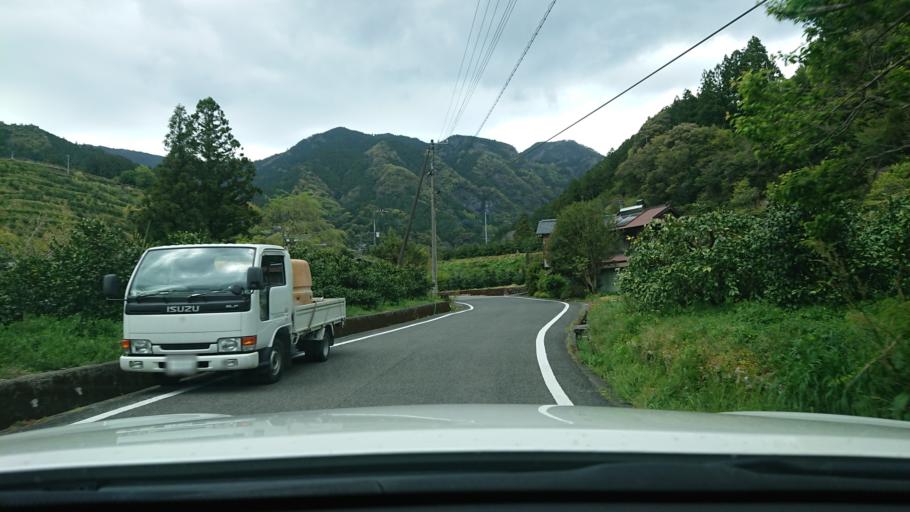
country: JP
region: Tokushima
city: Ishii
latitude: 33.9242
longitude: 134.4237
